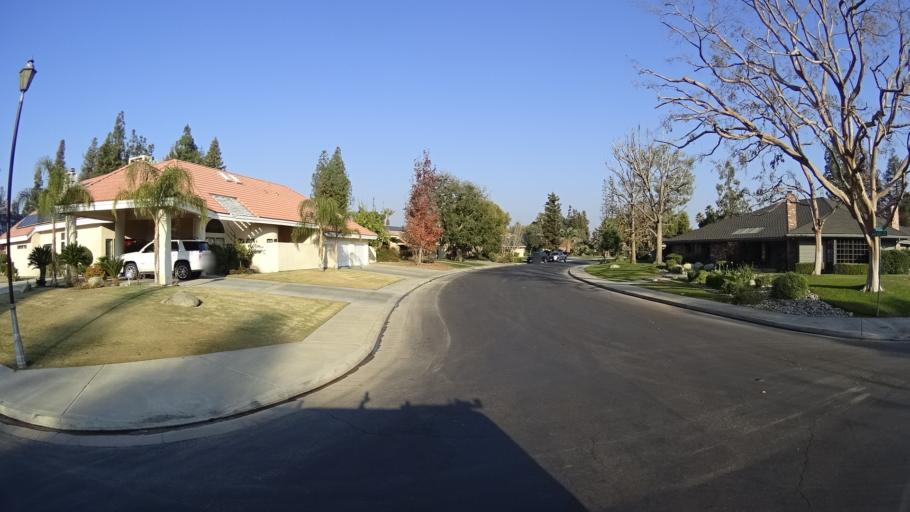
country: US
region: California
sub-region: Kern County
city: Greenacres
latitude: 35.3368
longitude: -119.0994
